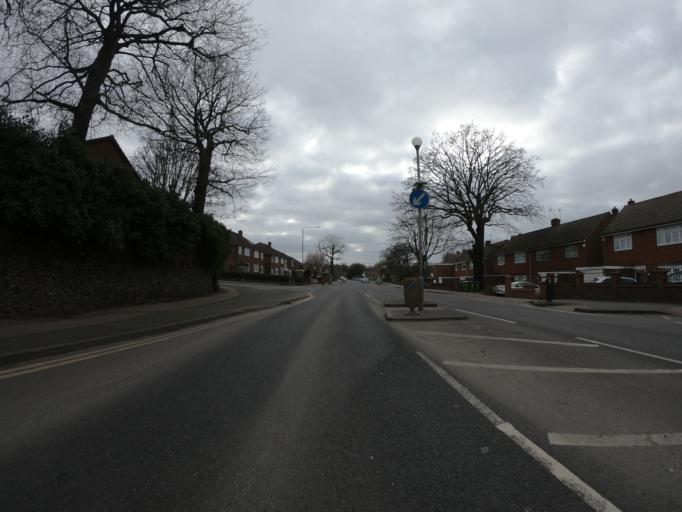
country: GB
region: England
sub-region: Greater London
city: Erith
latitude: 51.4800
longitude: 0.1677
